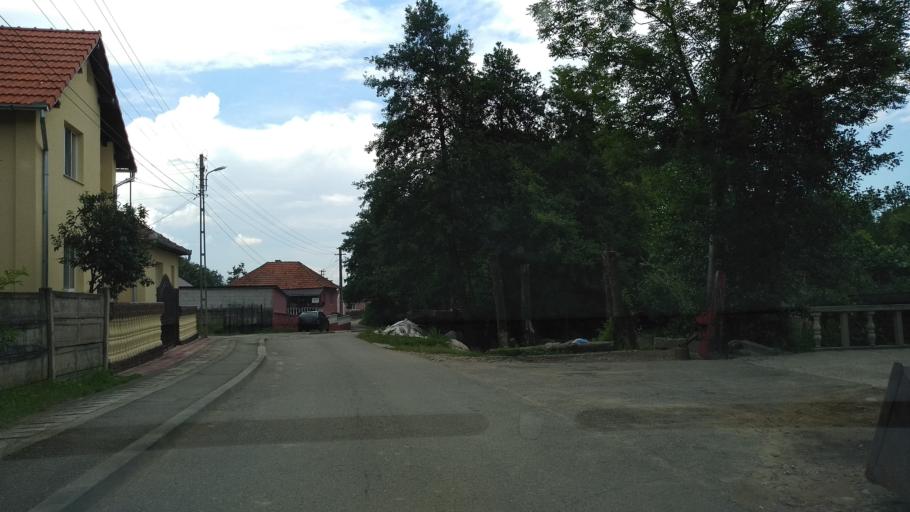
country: RO
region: Hunedoara
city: Salasu de Sus
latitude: 45.4889
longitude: 22.9446
